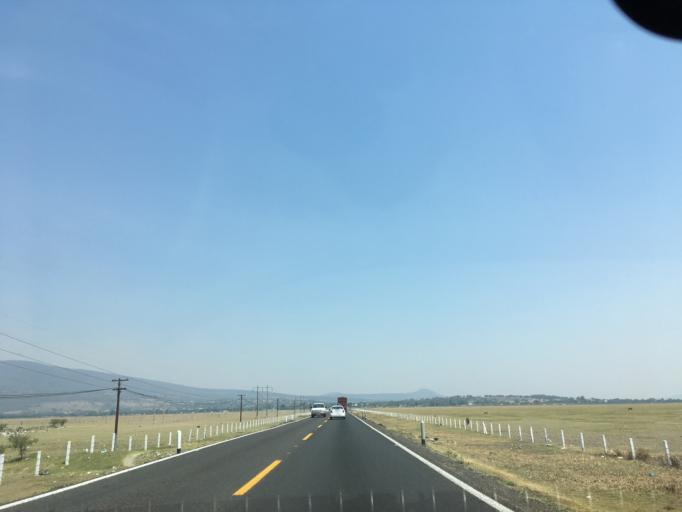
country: MX
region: Michoacan
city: Cuitzeo del Porvenir
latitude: 19.9764
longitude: -101.1413
